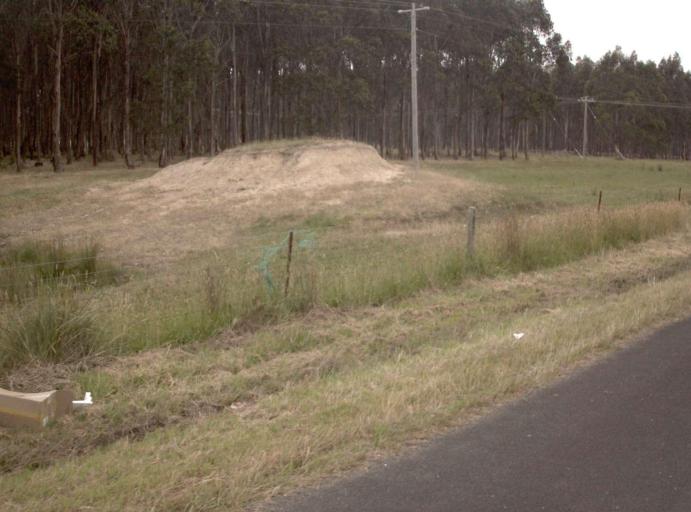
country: AU
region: Victoria
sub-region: Latrobe
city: Morwell
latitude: -38.2846
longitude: 146.4126
